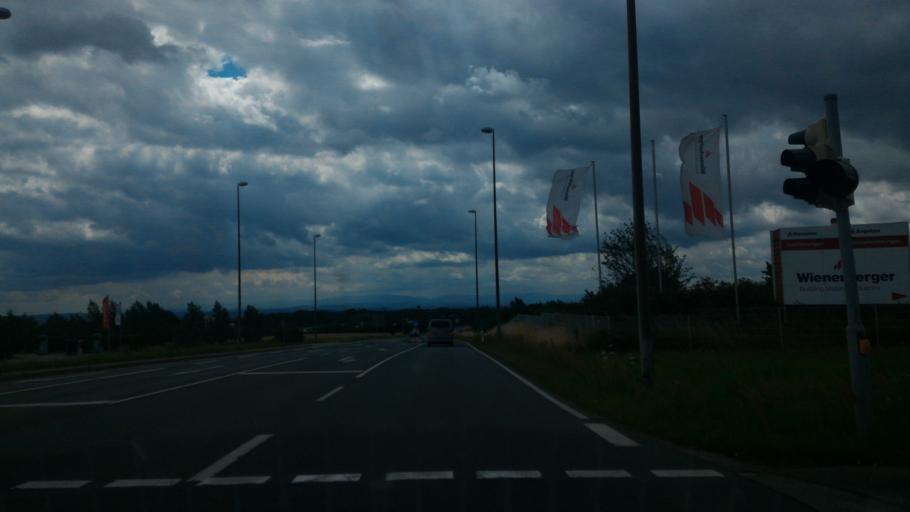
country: DE
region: Saxony
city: Goerlitz
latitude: 51.1878
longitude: 14.9569
